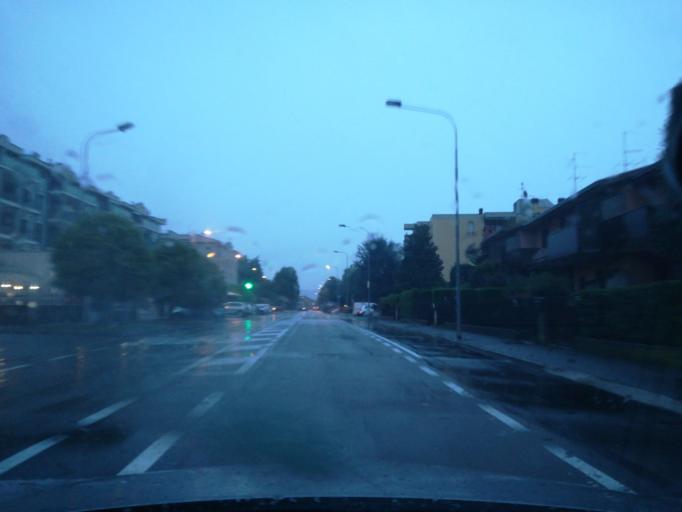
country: IT
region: Lombardy
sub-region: Provincia di Bergamo
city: Brembate di Sopra
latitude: 45.7172
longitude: 9.5775
